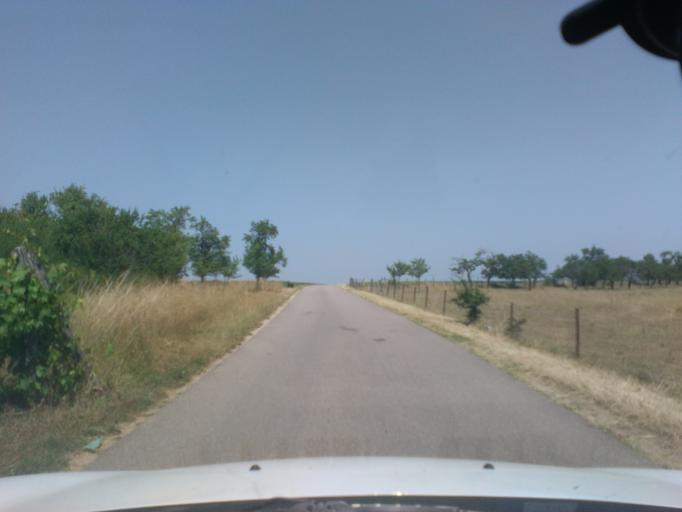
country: FR
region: Lorraine
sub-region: Departement des Vosges
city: Mirecourt
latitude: 48.3130
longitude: 6.1090
